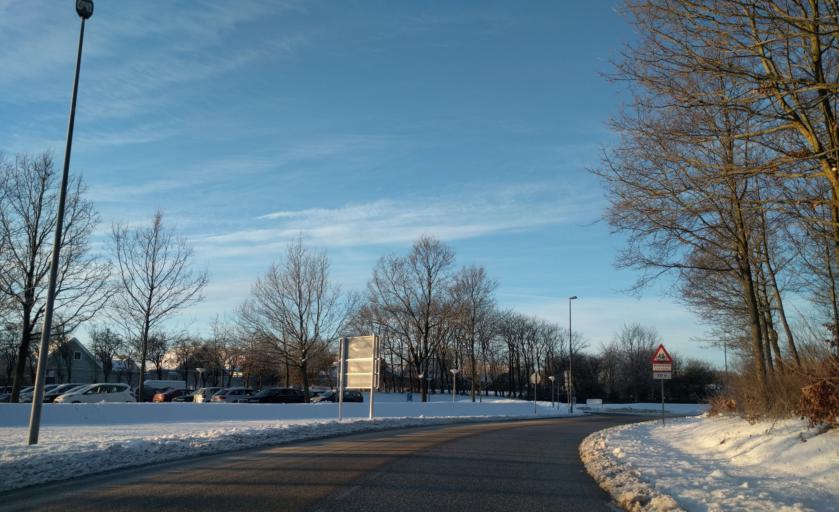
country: DK
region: North Denmark
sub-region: Alborg Kommune
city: Gistrup
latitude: 57.0189
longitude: 9.9752
